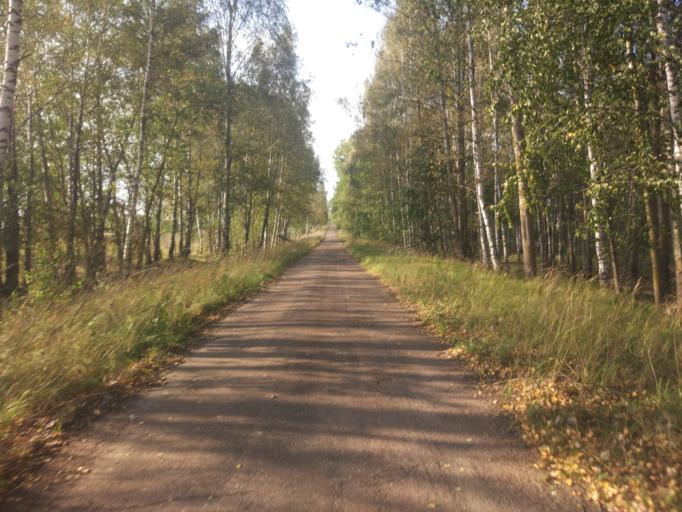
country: RU
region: Brjansk
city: Vyshkov
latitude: 52.6586
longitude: 31.5800
